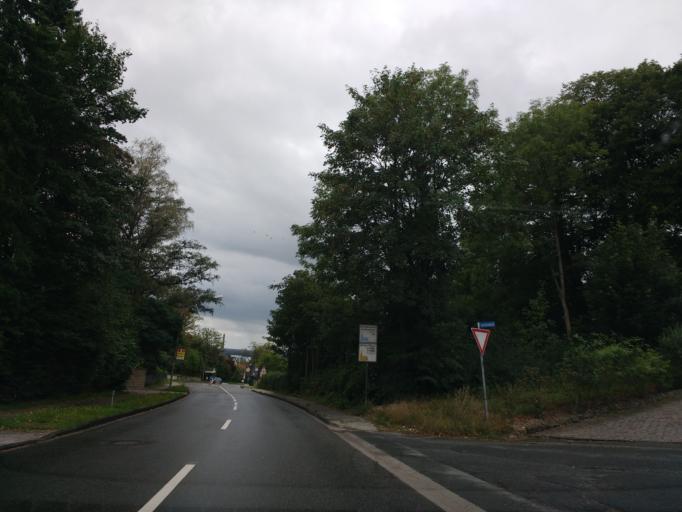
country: DE
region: North Rhine-Westphalia
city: Lengerich
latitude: 52.1936
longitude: 7.8591
